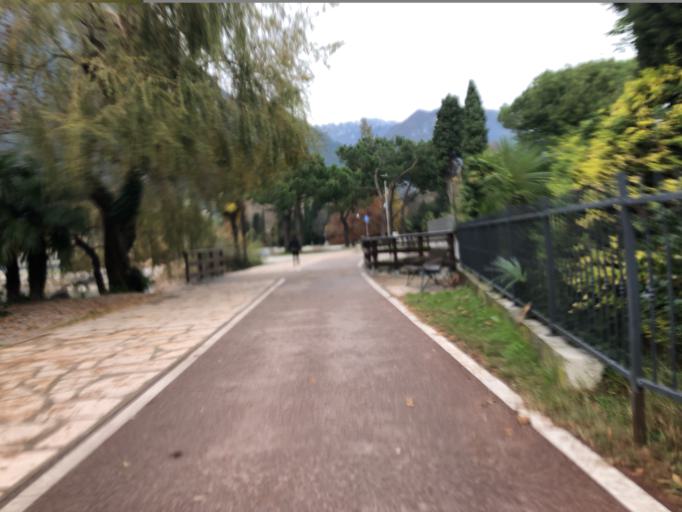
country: IT
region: Trentino-Alto Adige
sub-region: Provincia di Trento
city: Riva del Garda
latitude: 45.8804
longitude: 10.8503
